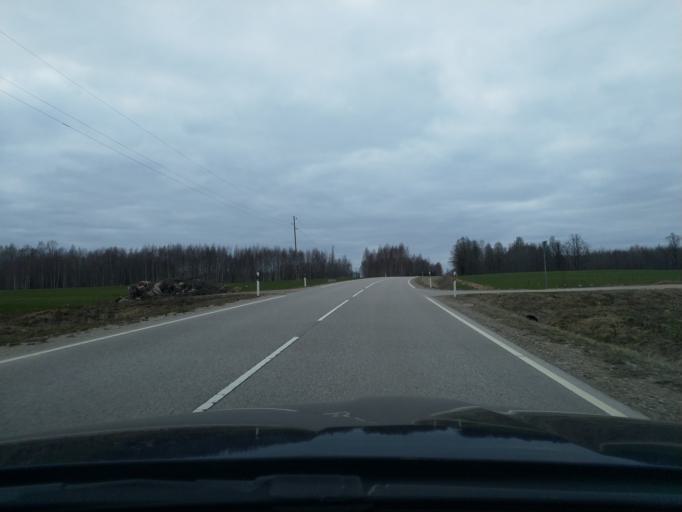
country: LV
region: Talsu Rajons
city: Sabile
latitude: 56.9449
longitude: 22.4818
